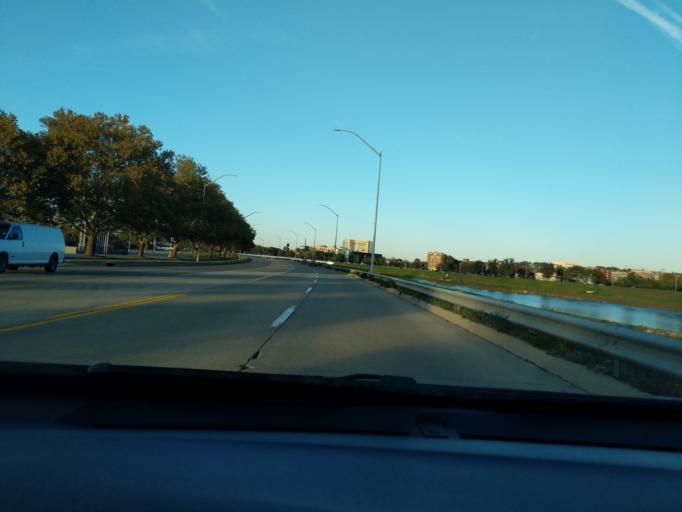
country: US
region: Ohio
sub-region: Montgomery County
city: Oakwood
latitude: 39.7345
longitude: -84.1974
